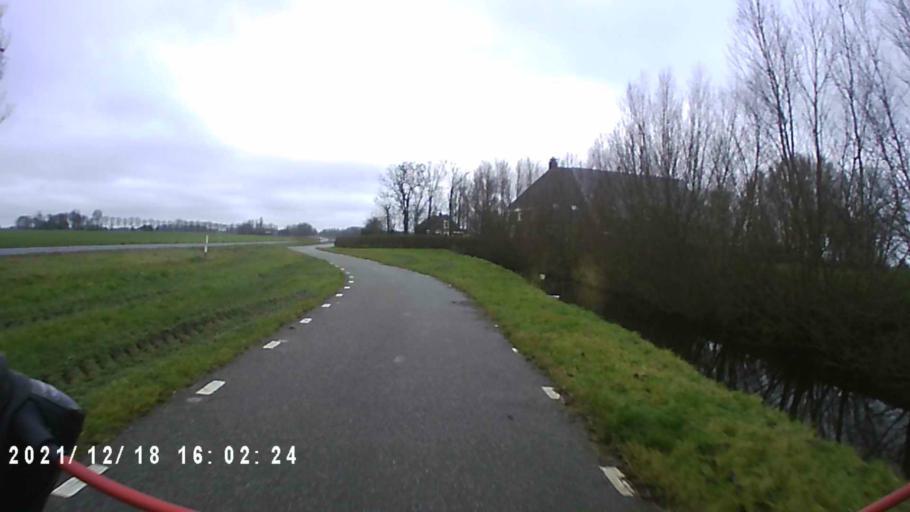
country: NL
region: Friesland
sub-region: Gemeente Dongeradeel
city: Anjum
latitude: 53.3472
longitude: 6.0839
